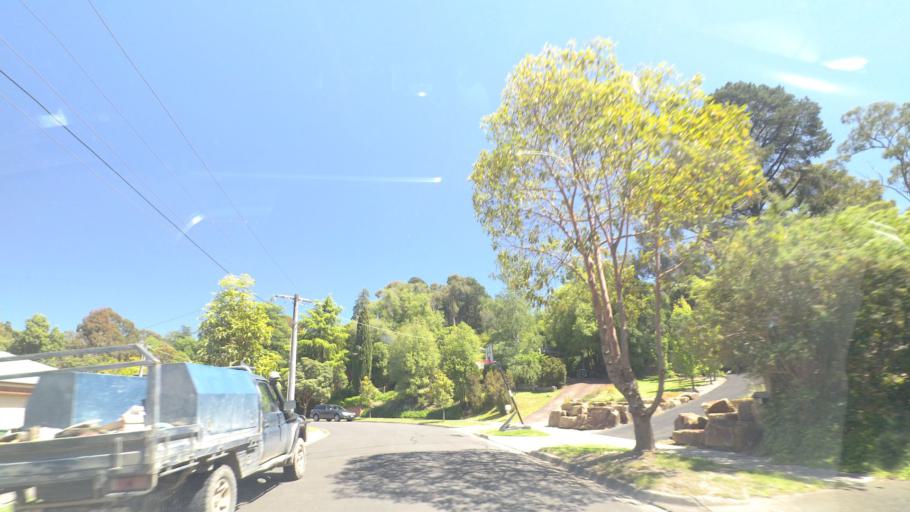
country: AU
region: Victoria
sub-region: Maroondah
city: Croydon North
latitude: -37.7768
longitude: 145.2830
